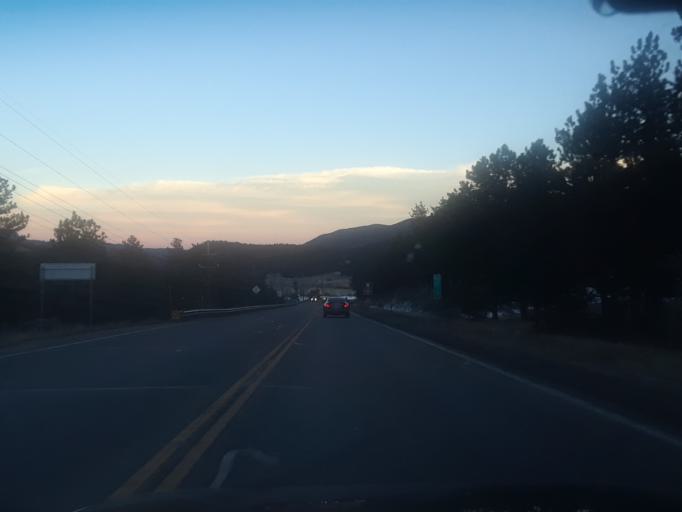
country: US
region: Colorado
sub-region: Clear Creek County
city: Georgetown
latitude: 39.4265
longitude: -105.5640
